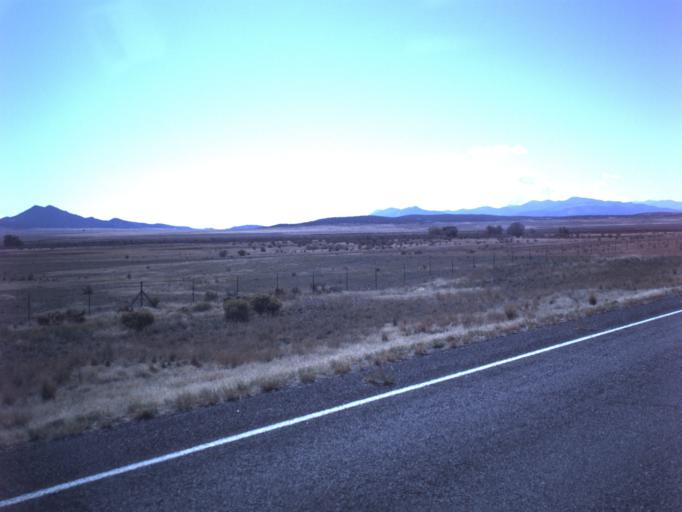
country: US
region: Utah
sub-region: Juab County
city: Nephi
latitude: 39.5105
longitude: -111.9481
